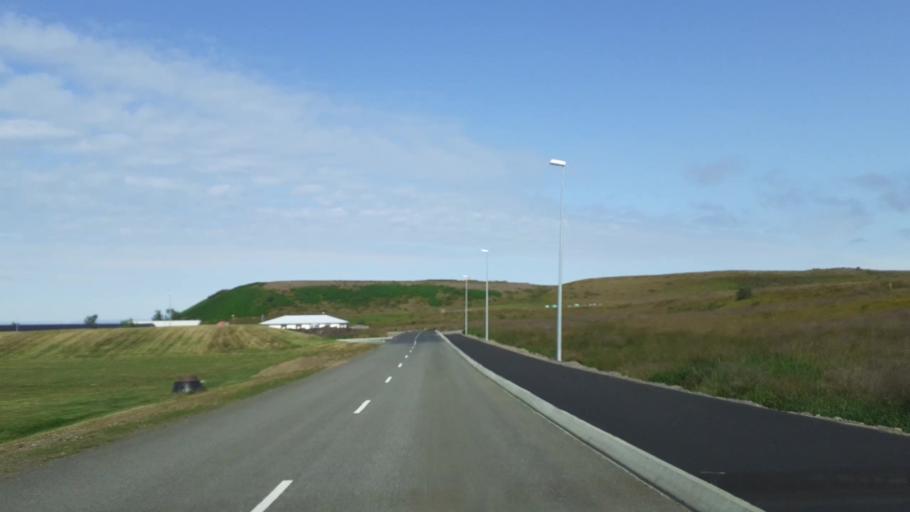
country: IS
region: Northwest
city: Saudarkrokur
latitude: 65.6632
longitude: -20.2833
